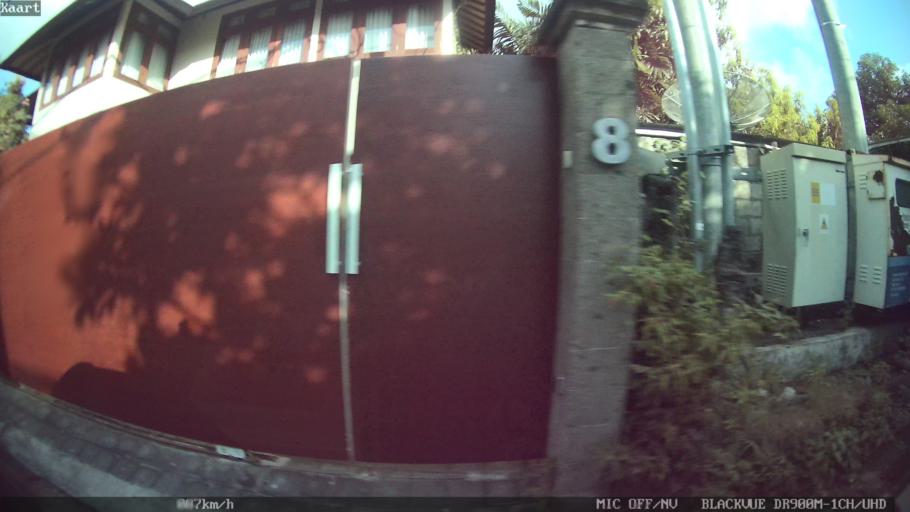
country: ID
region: Bali
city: Banjar Medura
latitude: -8.7059
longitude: 115.2495
